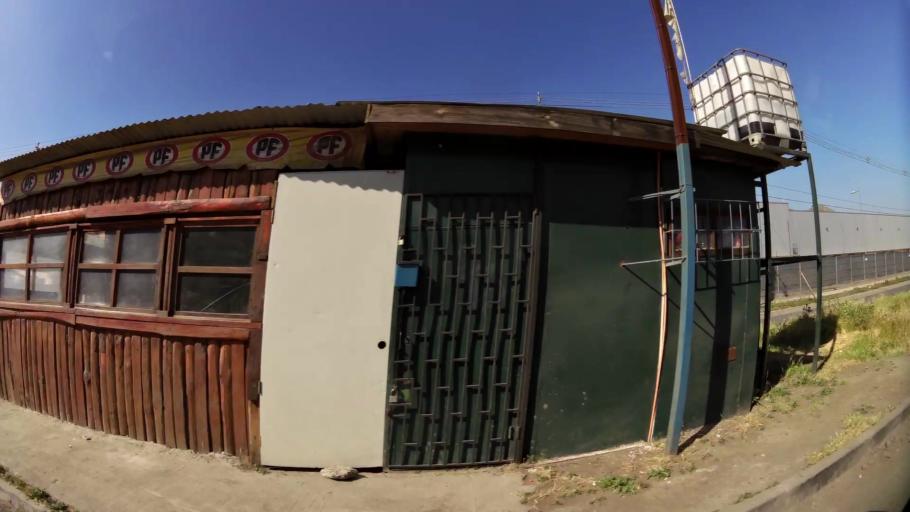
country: CL
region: Santiago Metropolitan
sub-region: Provincia de Chacabuco
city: Chicureo Abajo
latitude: -33.3352
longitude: -70.7043
